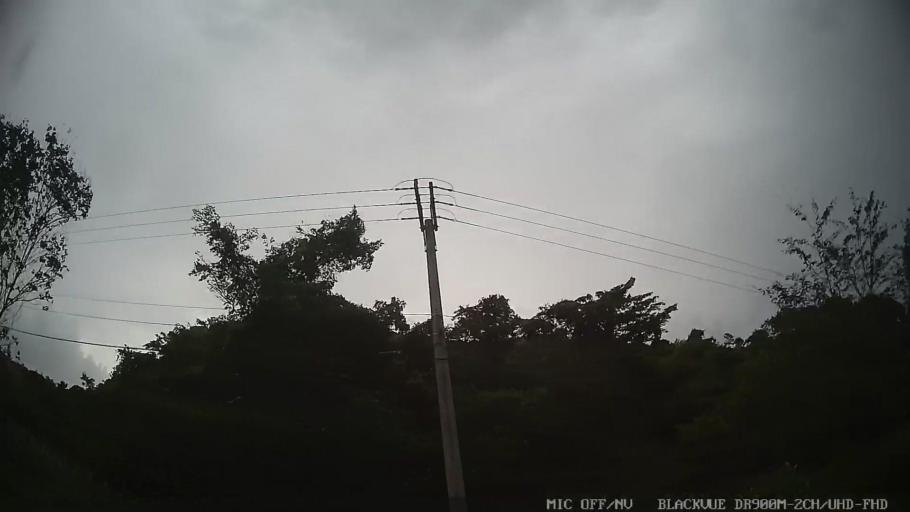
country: BR
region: Sao Paulo
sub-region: Pedreira
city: Pedreira
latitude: -22.7055
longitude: -46.8671
